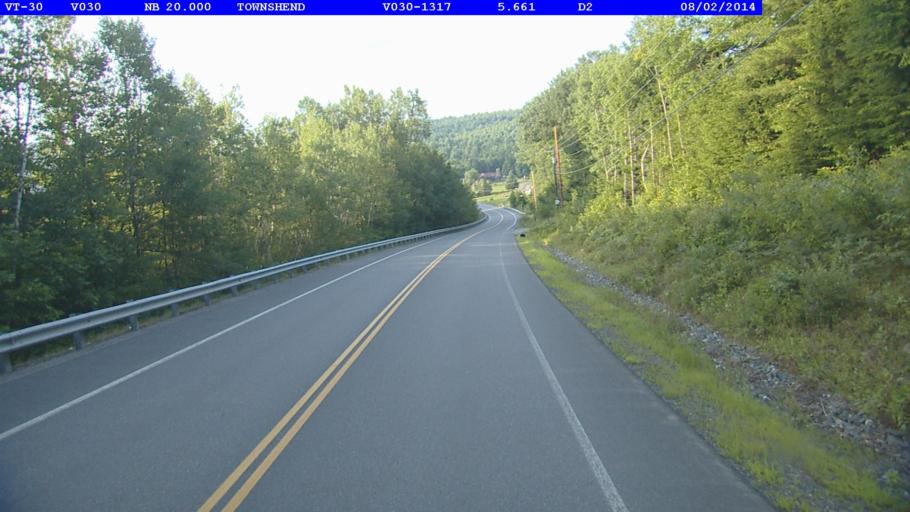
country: US
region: Vermont
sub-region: Windham County
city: Newfane
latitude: 43.0739
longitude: -72.7052
